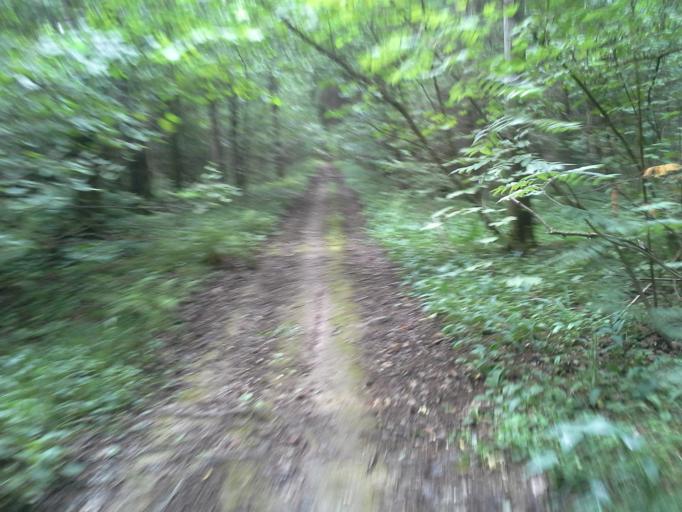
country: RU
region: Moskovskaya
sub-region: Leninskiy Rayon
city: Vnukovo
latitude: 55.6429
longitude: 37.2901
